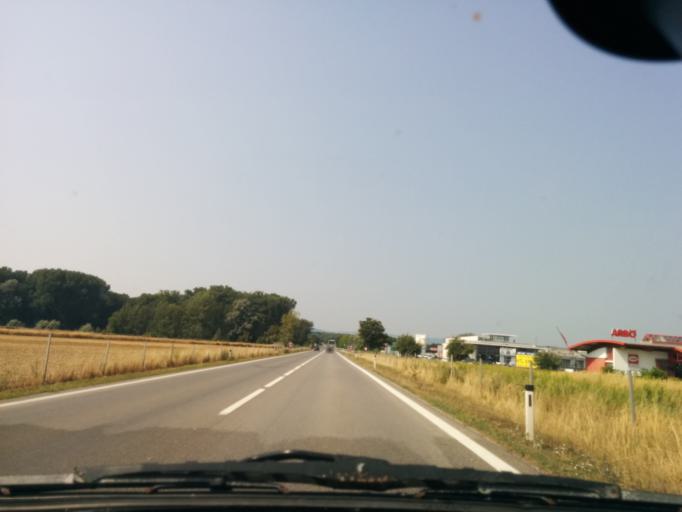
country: AT
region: Lower Austria
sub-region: Politischer Bezirk Krems
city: Gedersdorf
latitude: 48.4076
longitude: 15.6696
